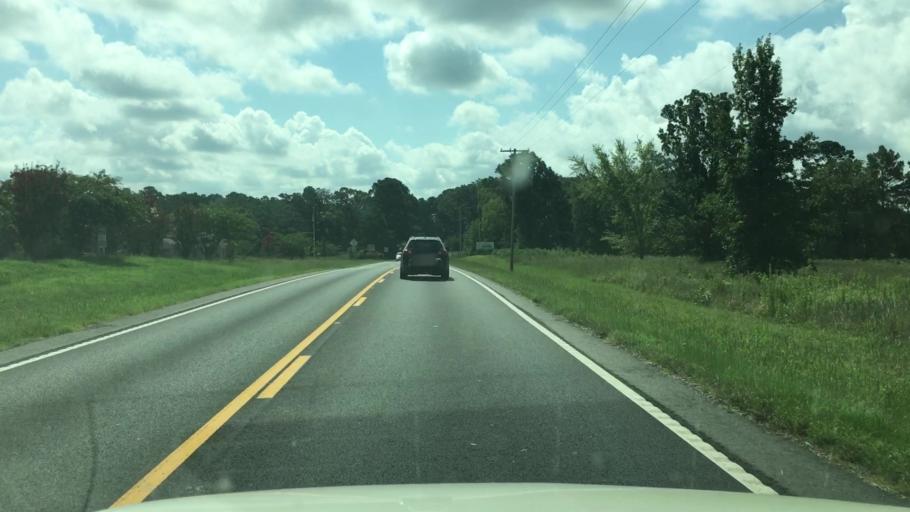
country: US
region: Arkansas
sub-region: Garland County
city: Lake Hamilton
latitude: 34.2814
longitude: -93.1615
